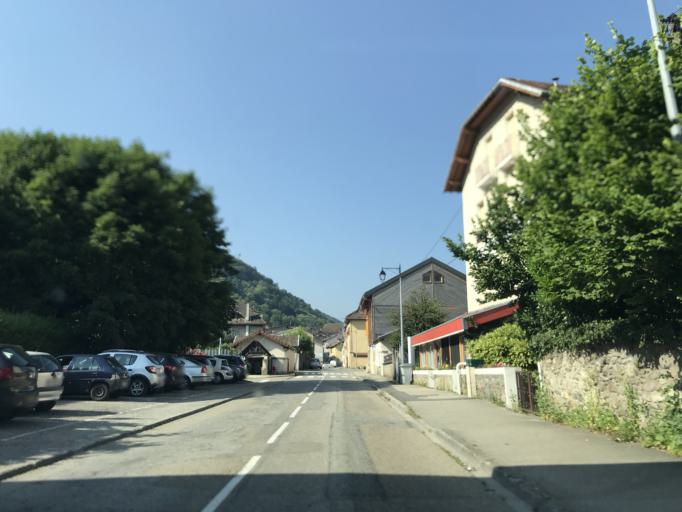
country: FR
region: Rhone-Alpes
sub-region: Departement de l'Isere
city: Allevard
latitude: 45.3956
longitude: 6.0772
